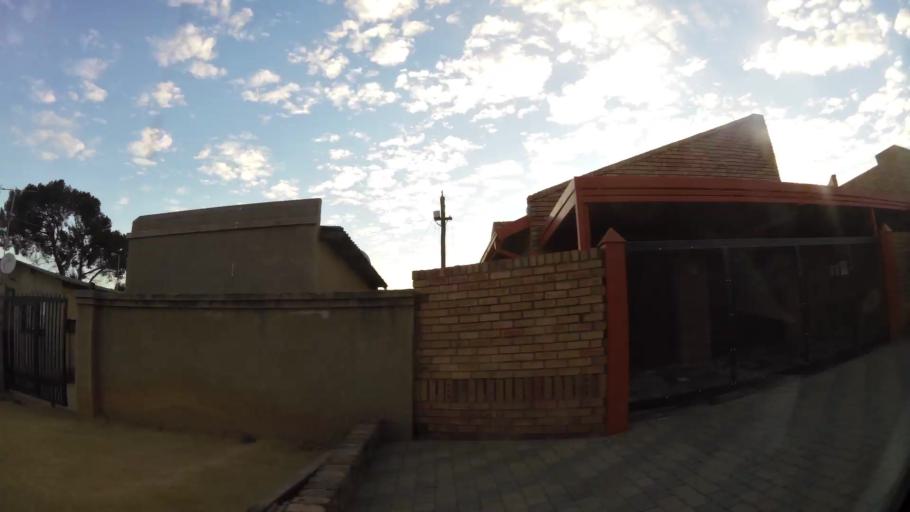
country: ZA
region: Gauteng
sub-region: City of Tshwane Metropolitan Municipality
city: Pretoria
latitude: -25.7172
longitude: 28.3488
